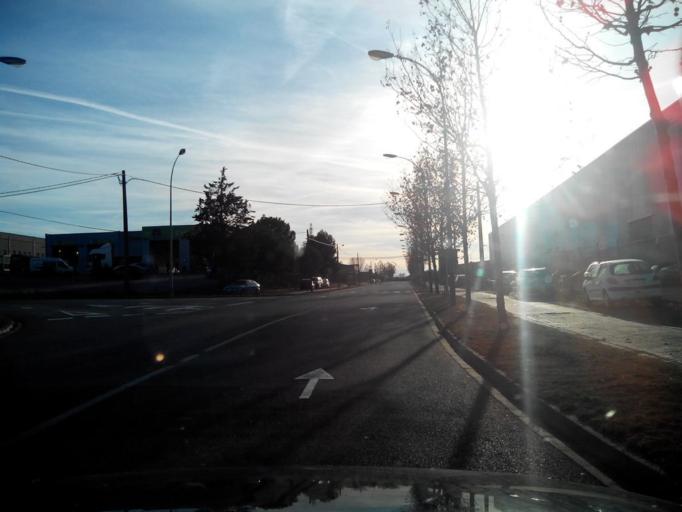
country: ES
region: Catalonia
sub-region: Provincia de Barcelona
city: Manresa
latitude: 41.7152
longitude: 1.8453
